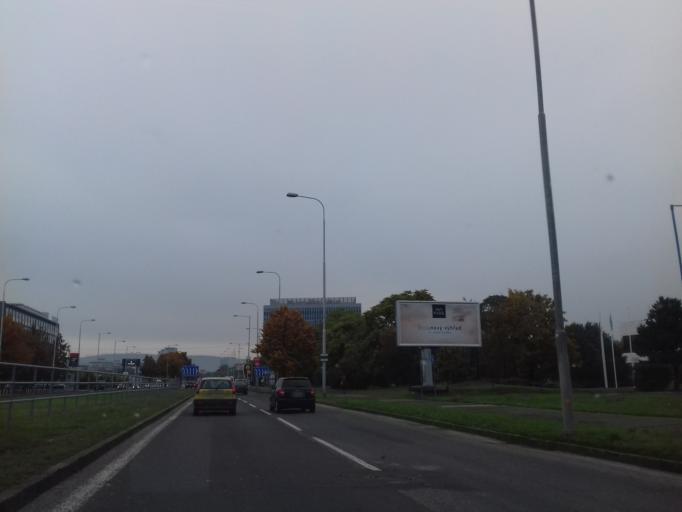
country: SK
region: Bratislavsky
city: Bratislava
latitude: 48.1519
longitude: 17.1480
